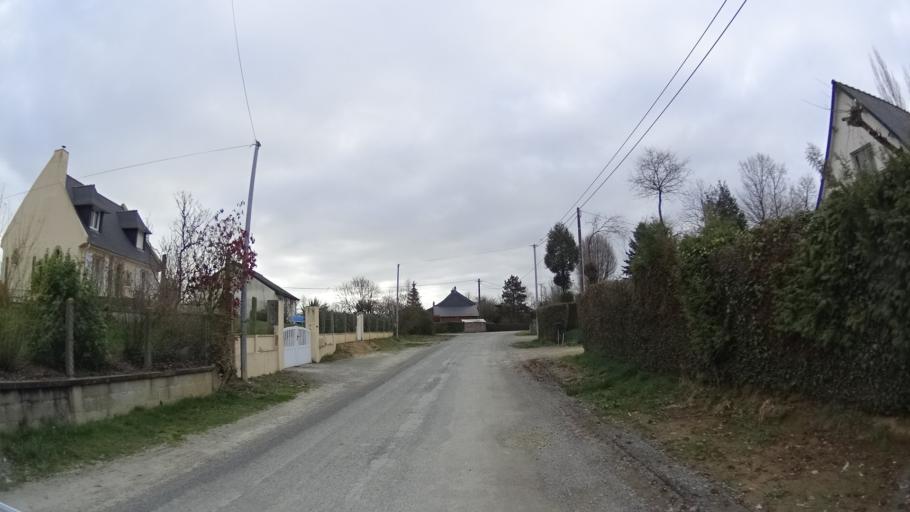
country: FR
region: Brittany
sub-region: Departement d'Ille-et-Vilaine
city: Saint-Gilles
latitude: 48.1816
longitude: -1.8615
